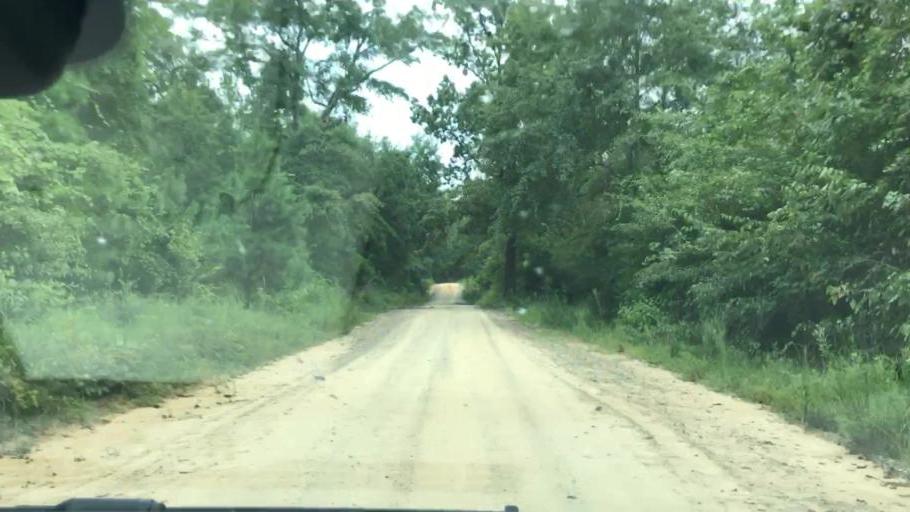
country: US
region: Georgia
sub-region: Clay County
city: Fort Gaines
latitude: 31.7252
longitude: -85.0749
